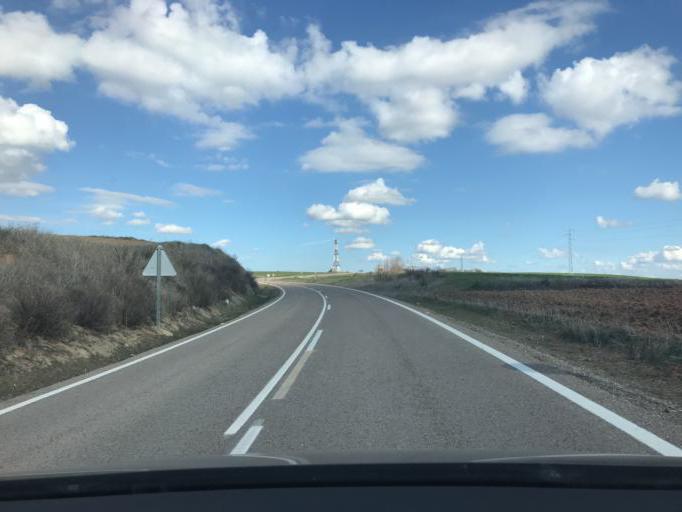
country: ES
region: Extremadura
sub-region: Provincia de Badajoz
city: Azuaga
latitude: 38.2564
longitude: -5.7271
